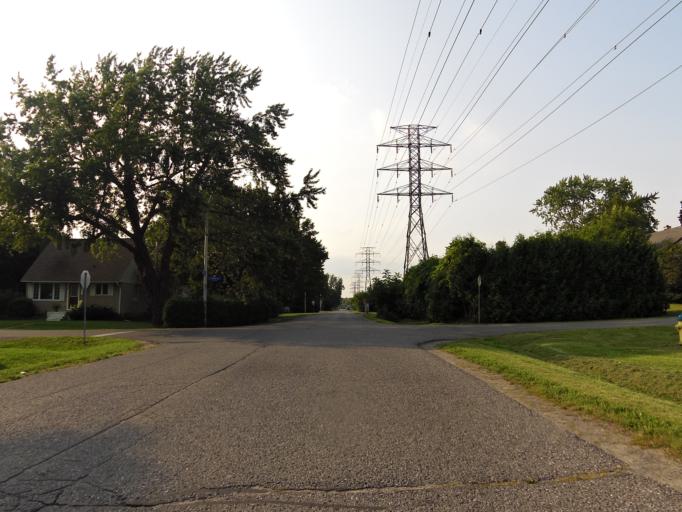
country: CA
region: Ontario
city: Ottawa
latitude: 45.3539
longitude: -75.7438
